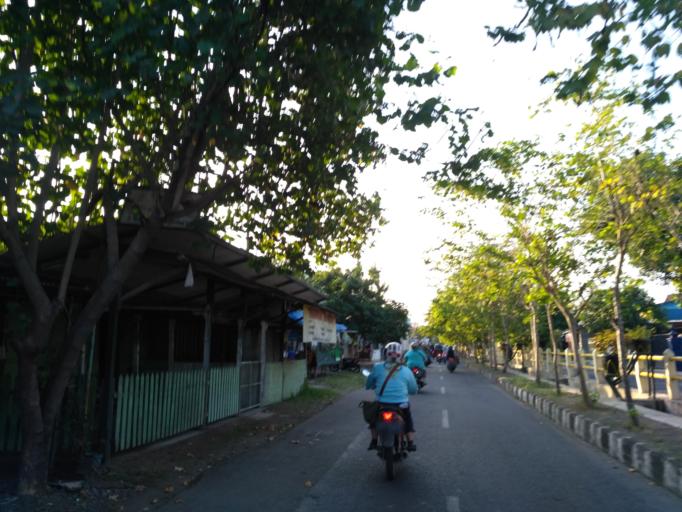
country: ID
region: Daerah Istimewa Yogyakarta
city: Yogyakarta
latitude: -7.8095
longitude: 110.3821
